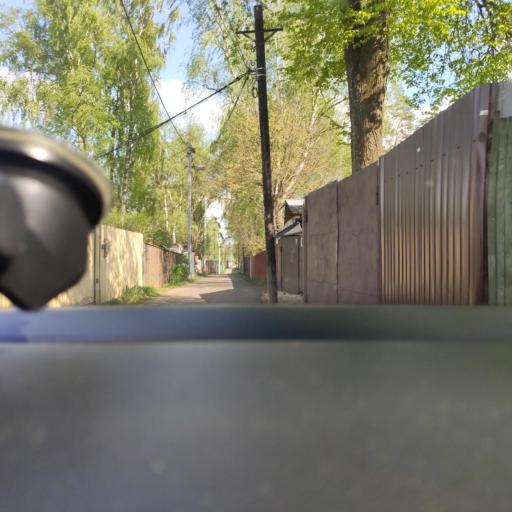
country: RU
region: Moskovskaya
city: Tomilino
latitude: 55.6459
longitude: 37.9472
